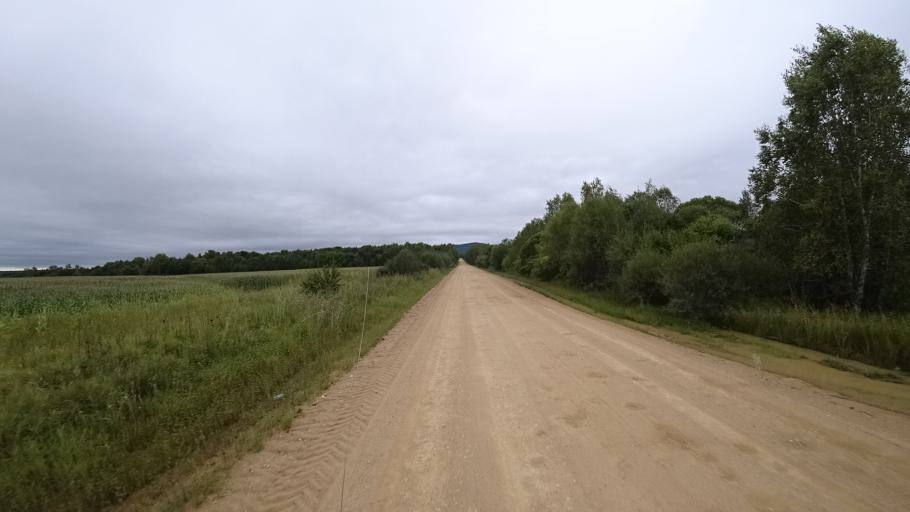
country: RU
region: Primorskiy
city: Rettikhovka
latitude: 44.1592
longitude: 132.7037
